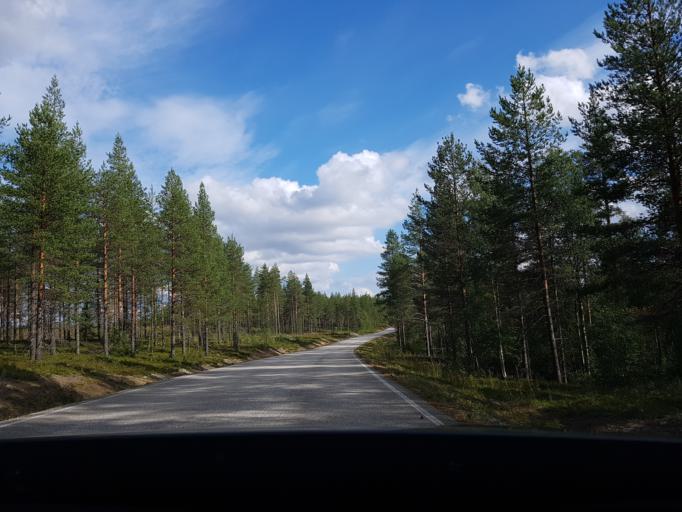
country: FI
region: Kainuu
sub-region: Kehys-Kainuu
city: Kuhmo
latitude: 64.6187
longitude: 29.7092
